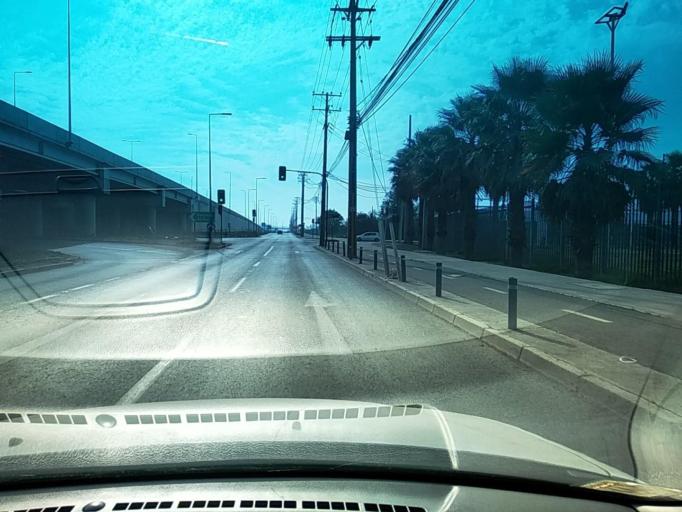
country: CL
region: Santiago Metropolitan
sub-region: Provincia de Chacabuco
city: Chicureo Abajo
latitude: -33.3263
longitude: -70.7174
